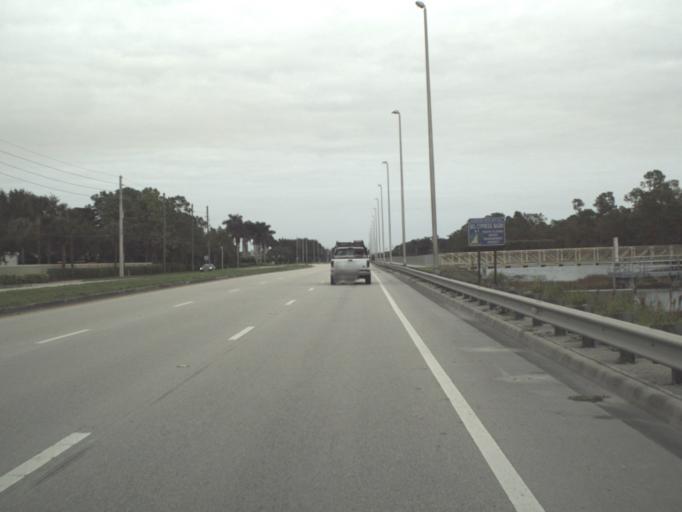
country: US
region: Florida
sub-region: Collier County
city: Golden Gate
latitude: 26.1388
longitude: -81.6867
